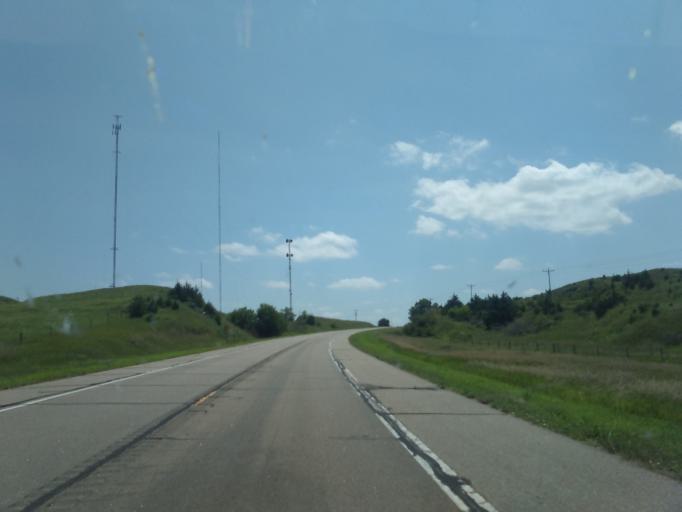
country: US
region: Nebraska
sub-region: Dawson County
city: Lexington
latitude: 40.7042
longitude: -99.7876
